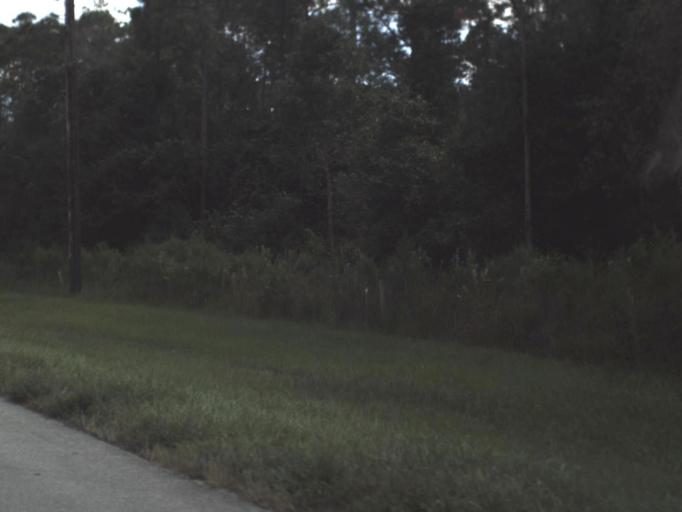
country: US
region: Florida
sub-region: Highlands County
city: Sebring
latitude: 27.4124
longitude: -81.5136
